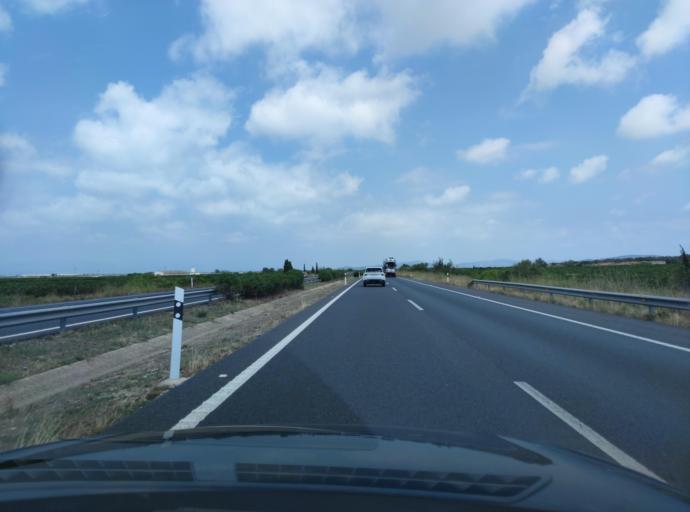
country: ES
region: Catalonia
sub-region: Provincia de Tarragona
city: Alcanar
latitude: 40.5122
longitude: 0.4154
